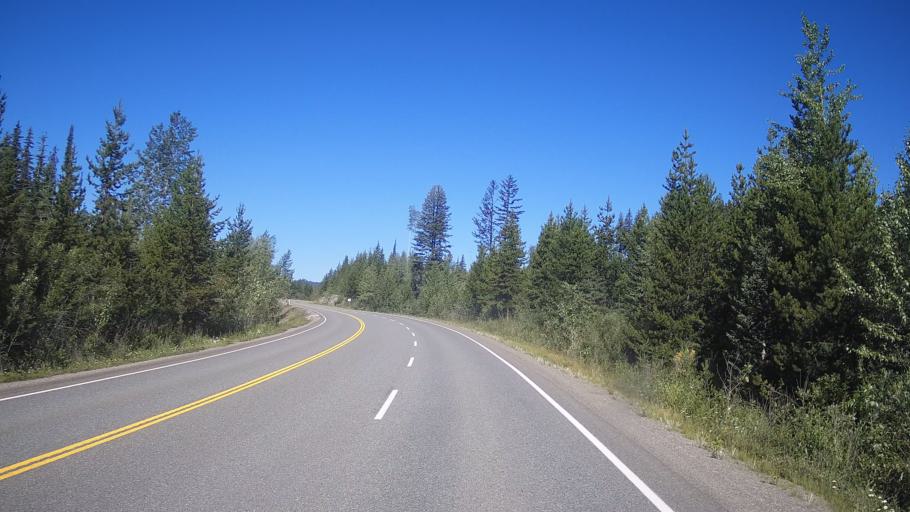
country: CA
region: British Columbia
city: Kamloops
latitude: 51.4937
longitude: -120.3290
